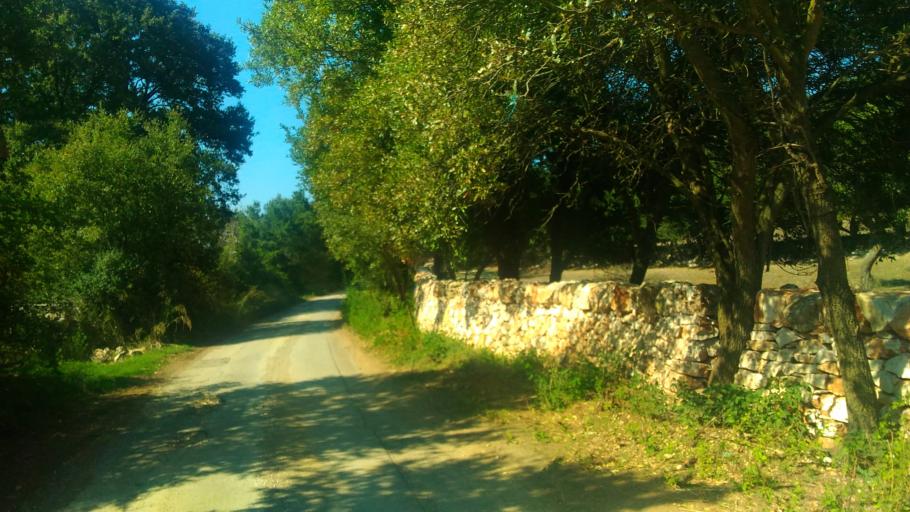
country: IT
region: Apulia
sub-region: Provincia di Bari
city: Noci
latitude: 40.8159
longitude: 17.1780
